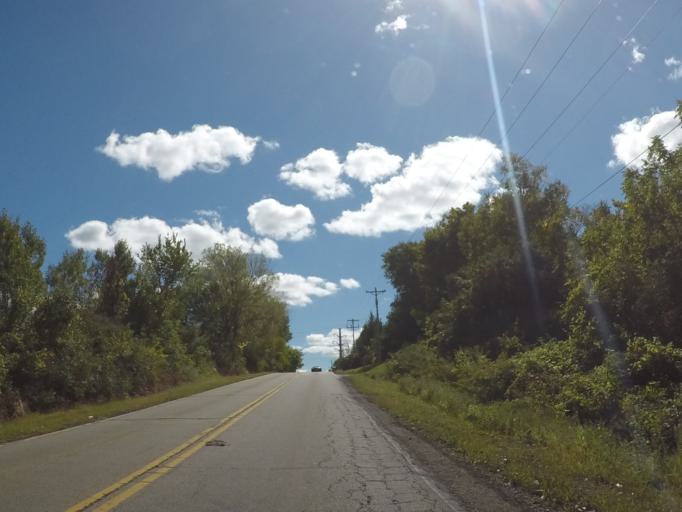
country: US
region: Wisconsin
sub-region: Dane County
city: Middleton
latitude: 43.0916
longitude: -89.5364
